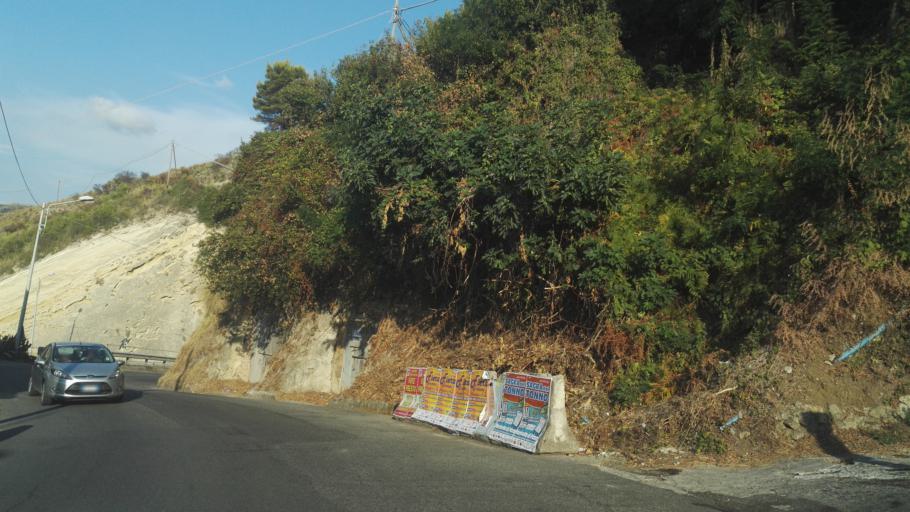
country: IT
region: Calabria
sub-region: Provincia di Vibo-Valentia
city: Pizzo
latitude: 38.7385
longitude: 16.1676
